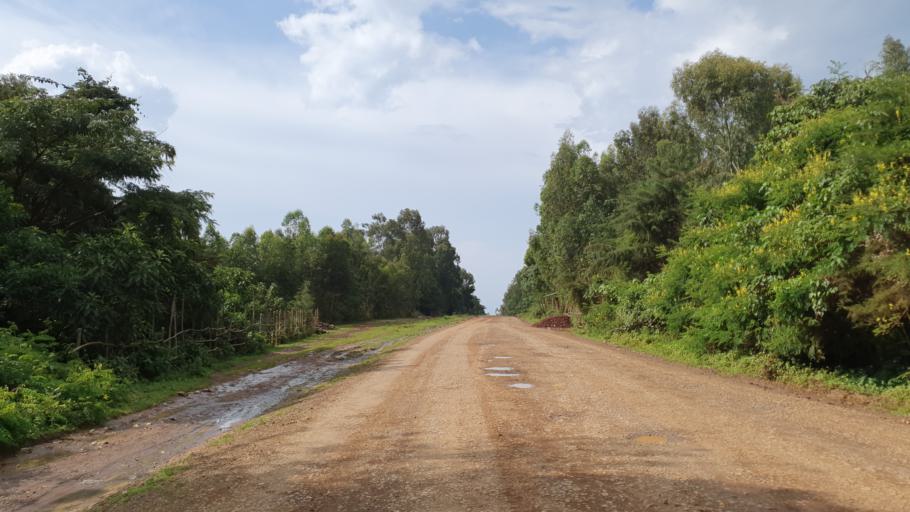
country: ET
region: Oromiya
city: Bedele
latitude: 9.1142
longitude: 36.5378
